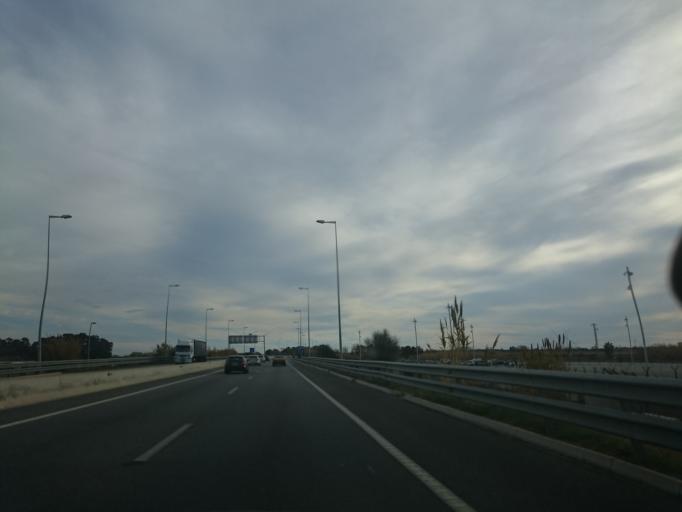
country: ES
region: Catalonia
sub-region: Provincia de Barcelona
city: Viladecans
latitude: 41.2888
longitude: 2.0517
